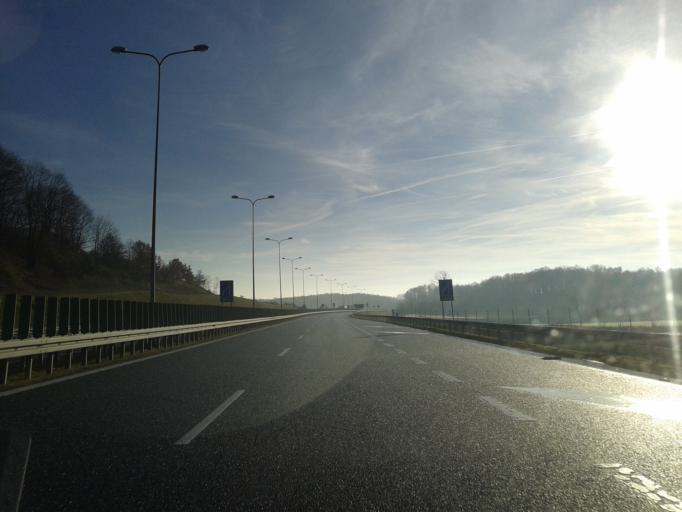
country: PL
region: Greater Poland Voivodeship
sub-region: Powiat pilski
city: Osiek nad Notecia
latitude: 53.1559
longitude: 17.3078
